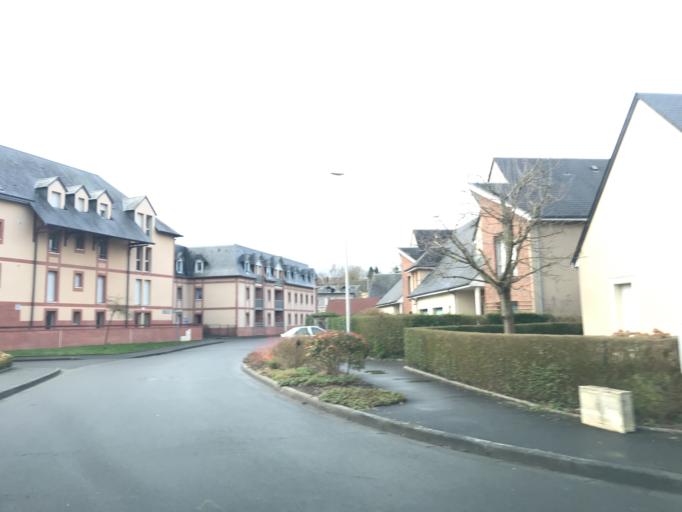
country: FR
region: Lower Normandy
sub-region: Departement du Calvados
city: Saint-Gatien-des-Bois
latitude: 49.2845
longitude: 0.1800
